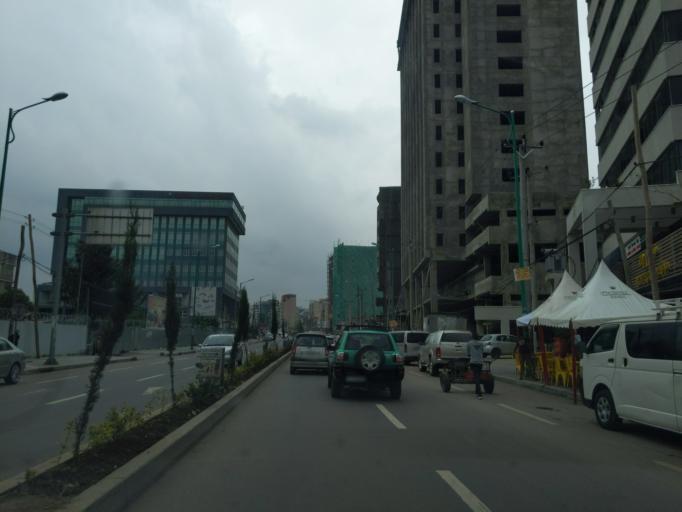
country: ET
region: Adis Abeba
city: Addis Ababa
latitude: 8.9886
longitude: 38.7653
